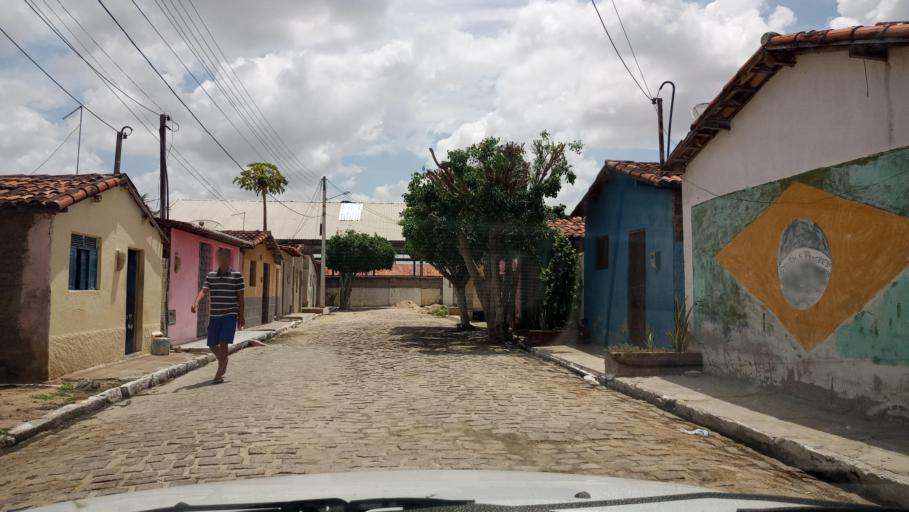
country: BR
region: Rio Grande do Norte
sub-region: Tangara
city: Tangara
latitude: -6.1039
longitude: -35.7140
